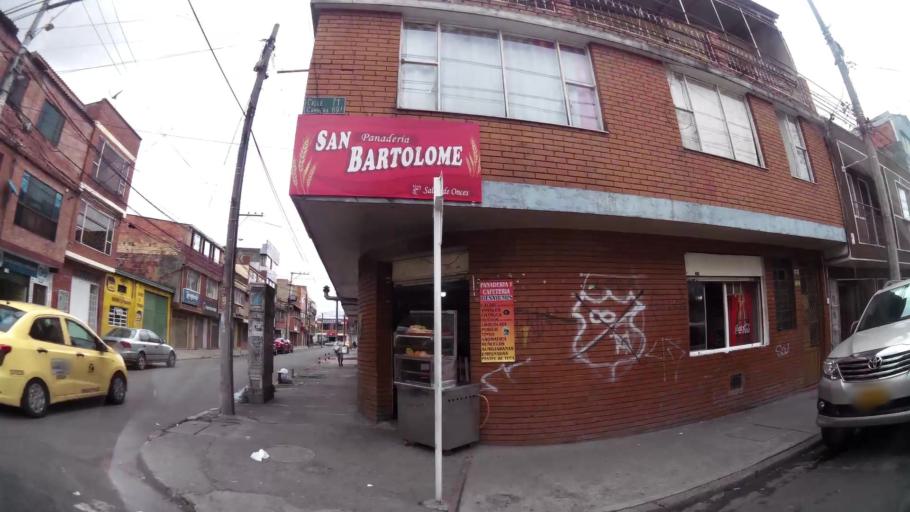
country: CO
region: Bogota D.C.
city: Barrio San Luis
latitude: 4.6815
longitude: -74.0908
